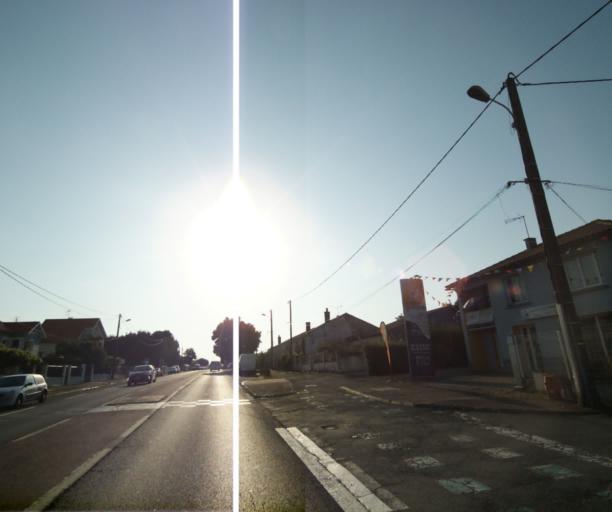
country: FR
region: Poitou-Charentes
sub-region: Departement de la Charente-Maritime
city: Tonnay-Charente
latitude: 45.9487
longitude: -0.9165
